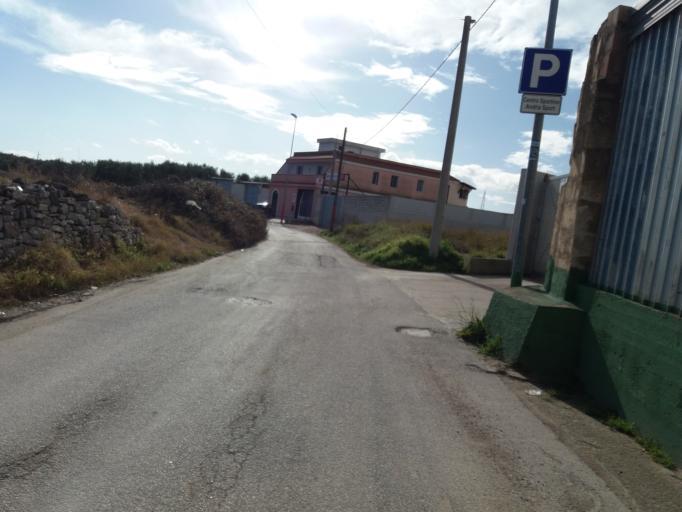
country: IT
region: Apulia
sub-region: Provincia di Barletta - Andria - Trani
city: Andria
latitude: 41.2165
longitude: 16.3055
